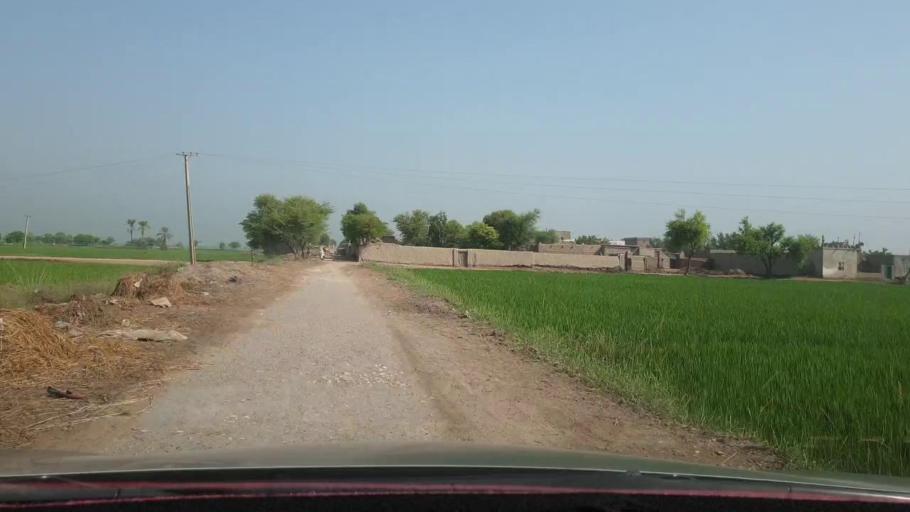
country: PK
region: Sindh
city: Kambar
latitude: 27.6011
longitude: 67.9362
